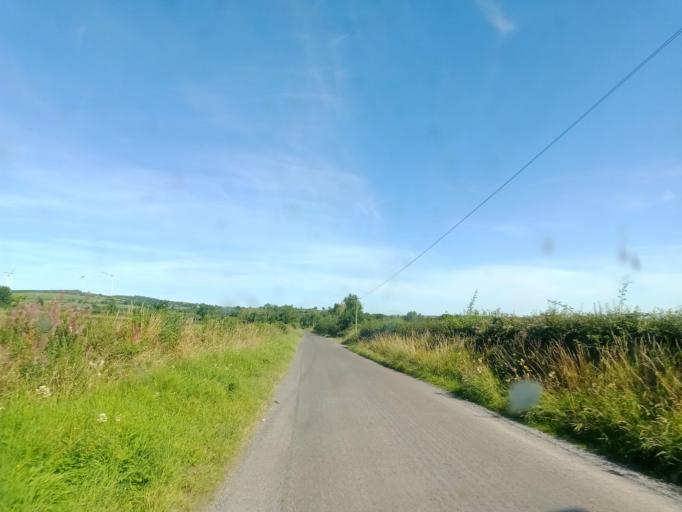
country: IE
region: Leinster
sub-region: Kilkenny
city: Ballyragget
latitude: 52.7688
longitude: -7.4102
